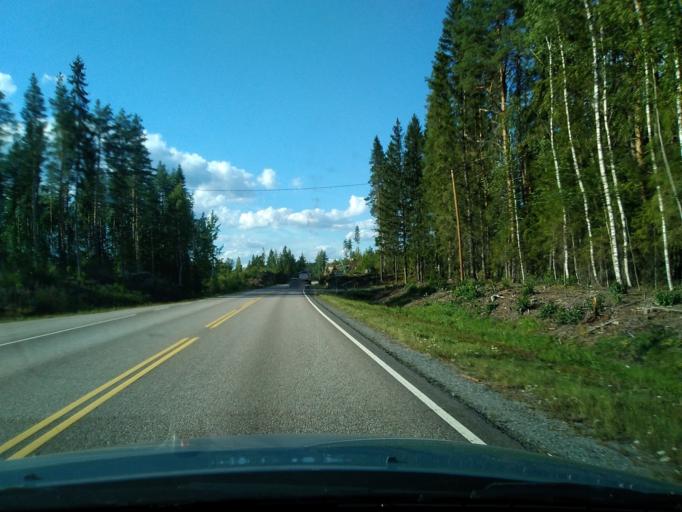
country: FI
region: Pirkanmaa
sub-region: Ylae-Pirkanmaa
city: Maenttae
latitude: 62.1210
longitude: 24.7416
